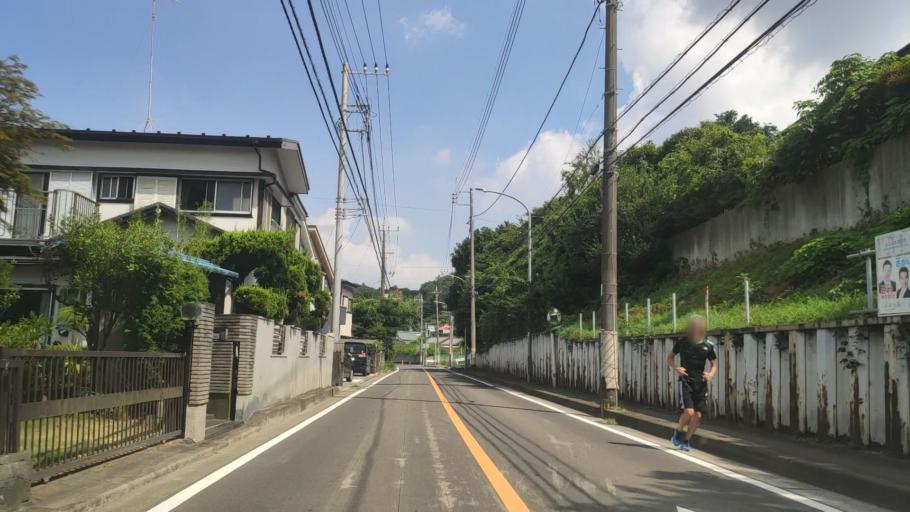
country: JP
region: Kanagawa
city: Minami-rinkan
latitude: 35.4417
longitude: 139.5074
